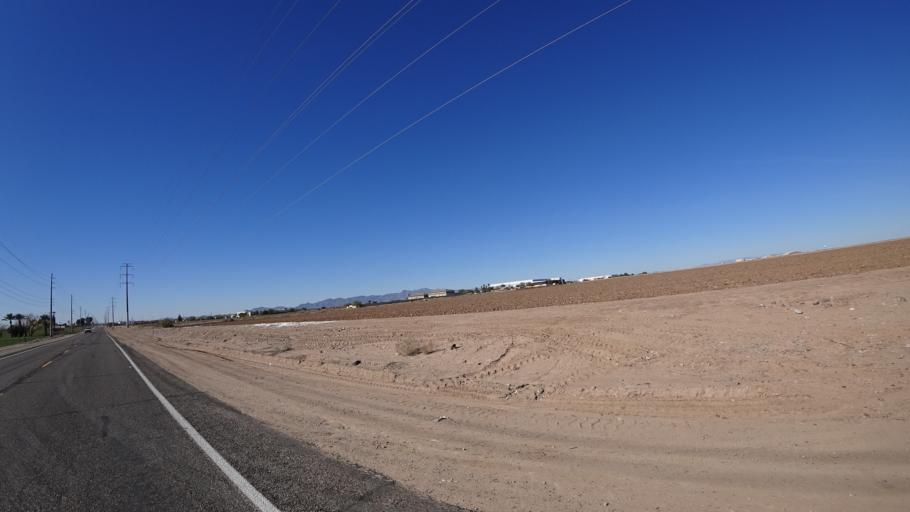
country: US
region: Arizona
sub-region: Maricopa County
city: Goodyear
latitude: 33.4065
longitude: -112.3686
